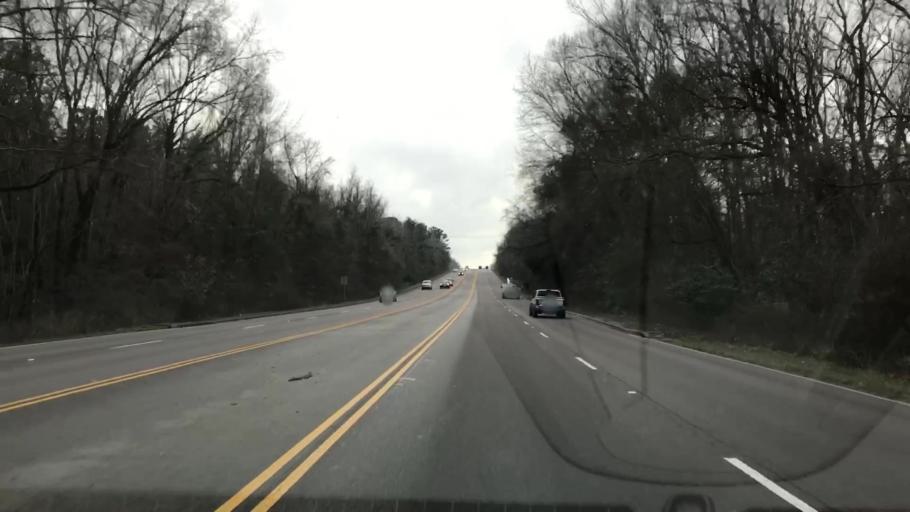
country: US
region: South Carolina
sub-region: Berkeley County
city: Moncks Corner
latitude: 33.2184
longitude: -79.9704
